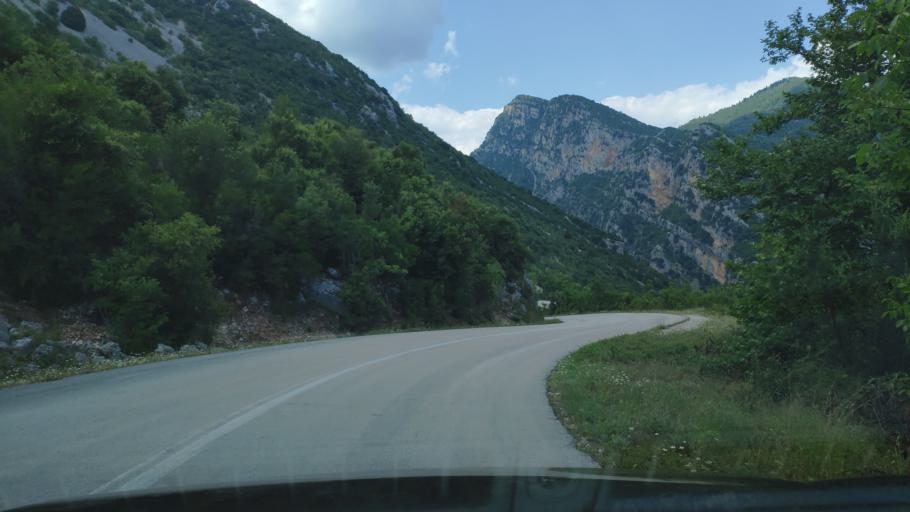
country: GR
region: Epirus
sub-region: Nomos Artas
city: Agios Dimitrios
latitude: 39.4640
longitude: 21.0222
